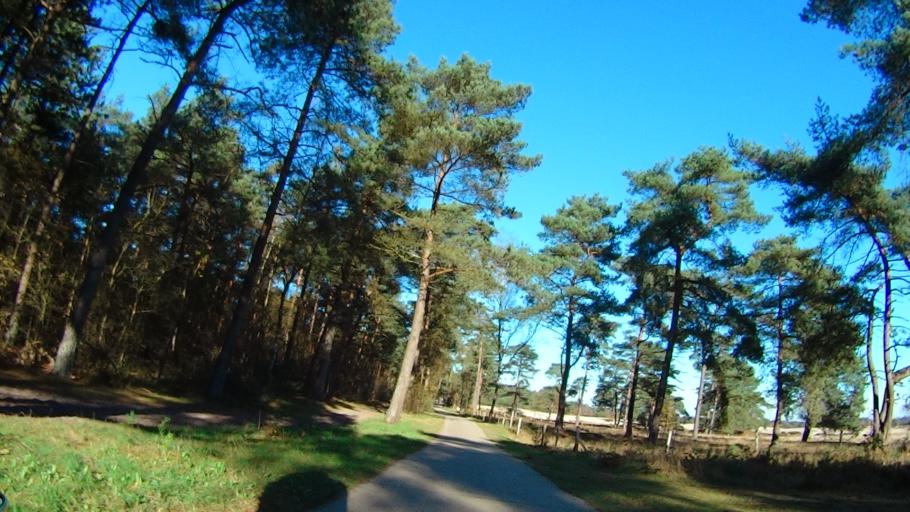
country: NL
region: Utrecht
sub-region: Gemeente Soest
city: Soest
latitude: 52.1510
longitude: 5.2851
